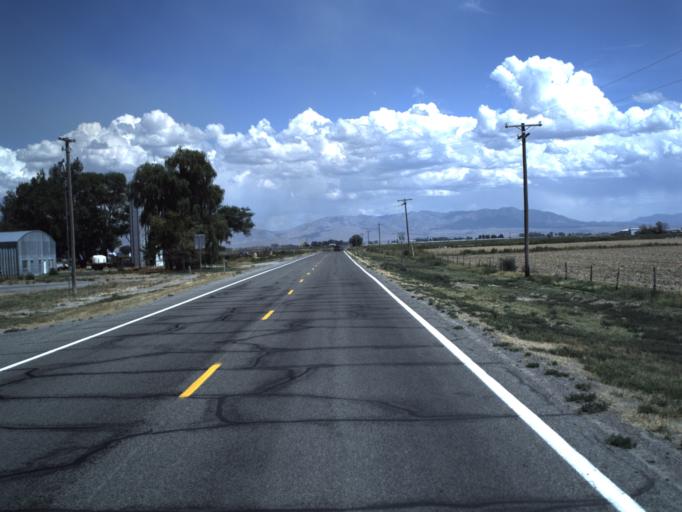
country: US
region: Utah
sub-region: Millard County
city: Delta
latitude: 39.3307
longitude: -112.6612
